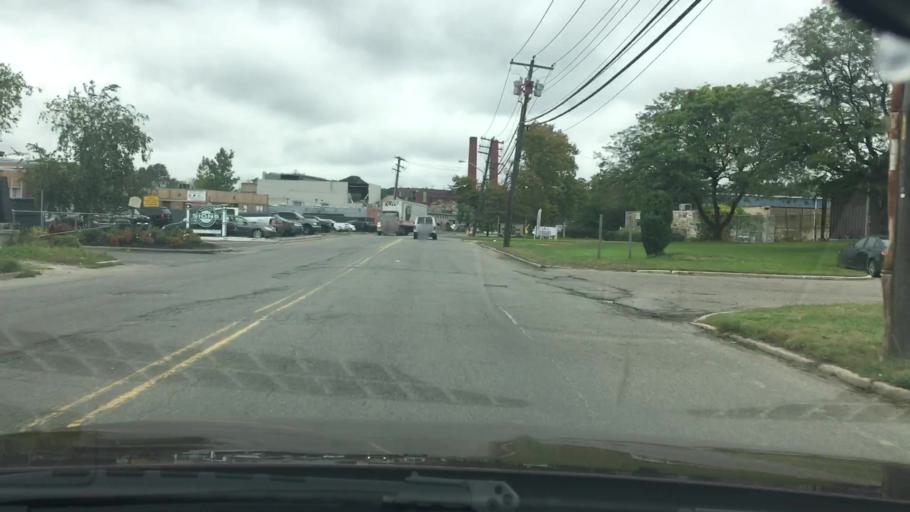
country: US
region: New York
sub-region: Nassau County
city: Old Bethpage
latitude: 40.7616
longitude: -73.4417
